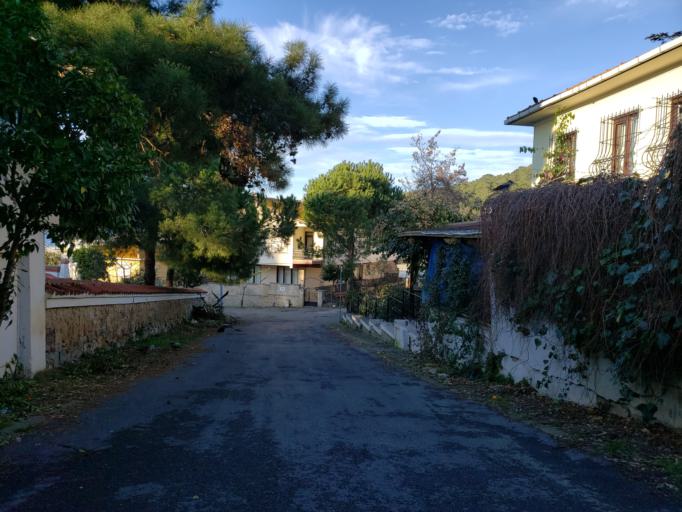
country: TR
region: Istanbul
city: Adalan
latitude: 40.8792
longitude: 29.0914
